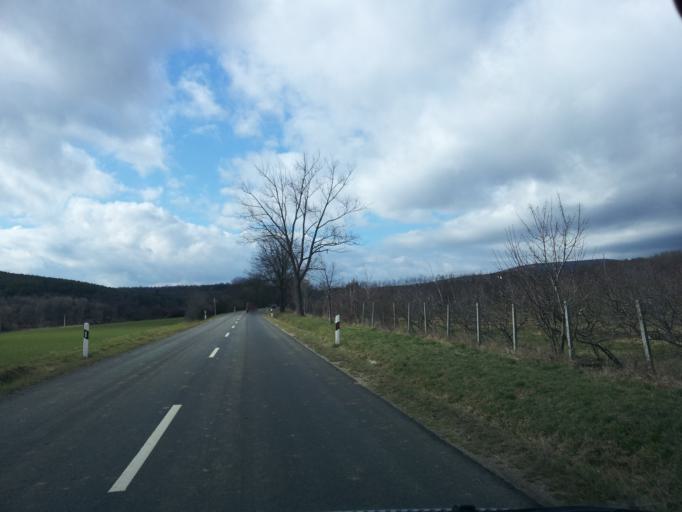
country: HU
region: Vas
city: Koszeg
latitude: 47.3448
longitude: 16.5344
